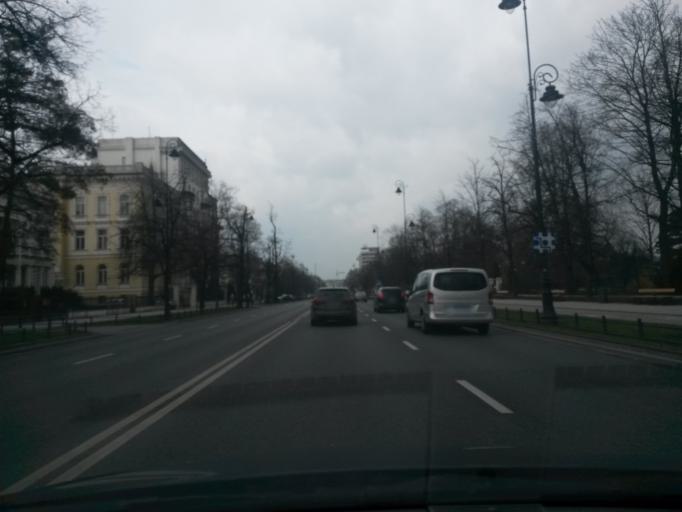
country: PL
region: Masovian Voivodeship
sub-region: Warszawa
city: Srodmiescie
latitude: 52.2214
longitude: 21.0247
